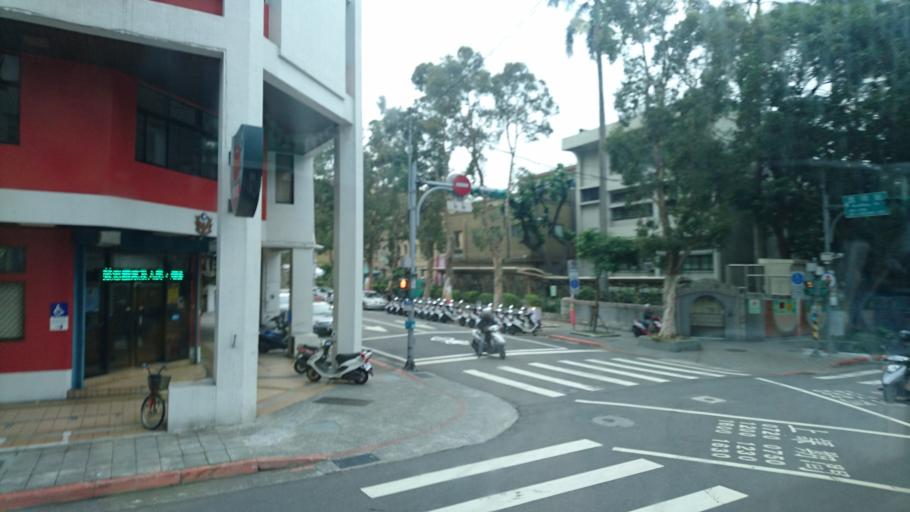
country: TW
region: Taipei
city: Taipei
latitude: 25.0377
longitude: 121.5039
